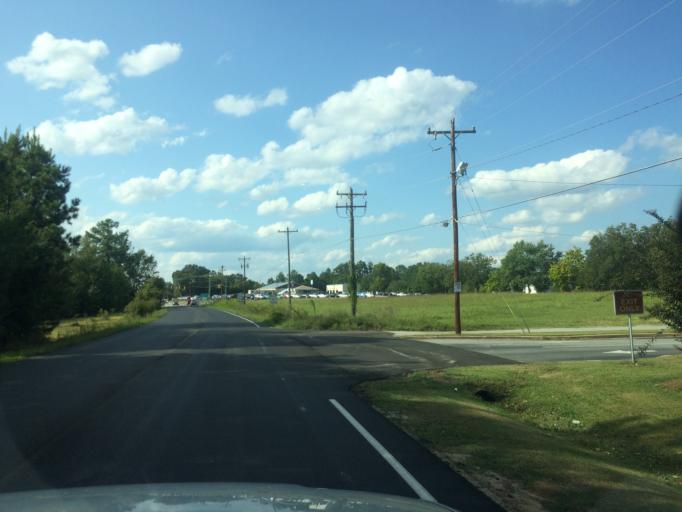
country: US
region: South Carolina
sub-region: Greenwood County
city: Ware Shoals
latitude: 34.5194
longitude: -82.1880
